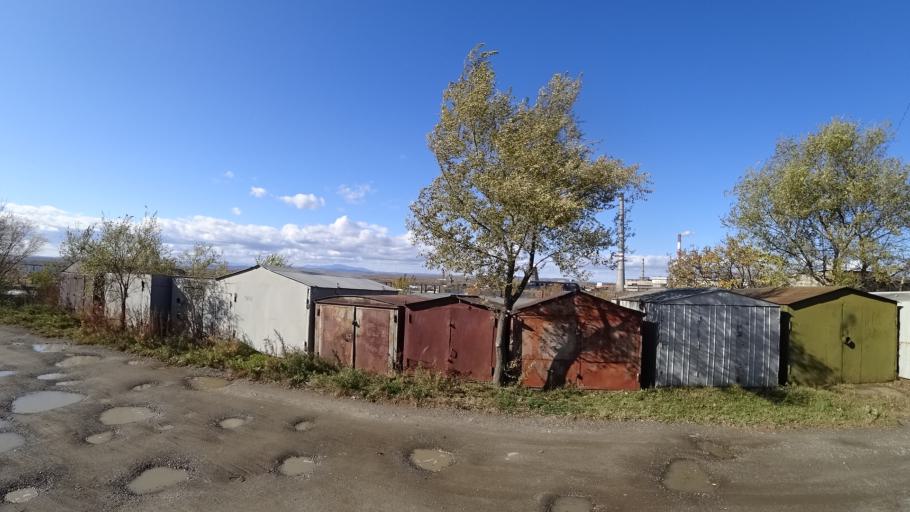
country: RU
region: Khabarovsk Krai
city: Amursk
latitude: 50.2176
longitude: 136.8898
